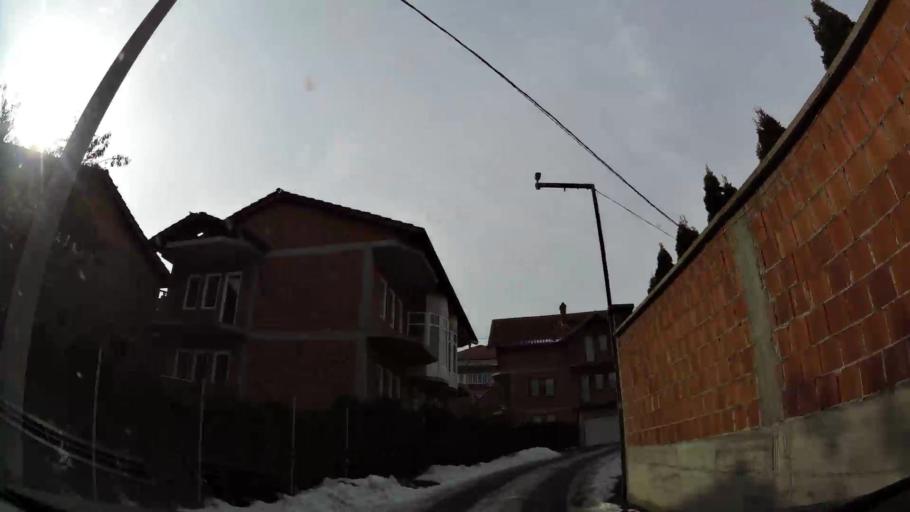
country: XK
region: Pristina
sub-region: Komuna e Prishtines
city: Pristina
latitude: 42.6800
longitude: 21.1616
